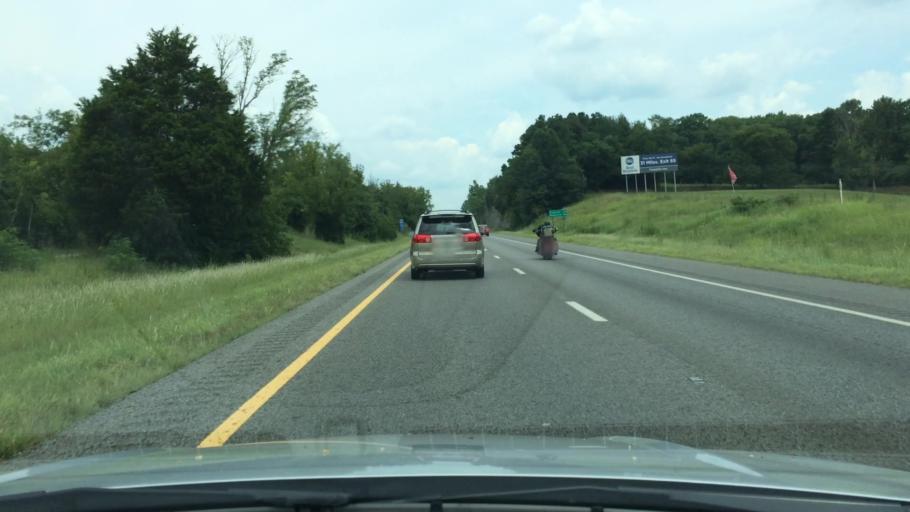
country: US
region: Tennessee
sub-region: Marshall County
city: Lewisburg
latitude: 35.4612
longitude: -86.8862
